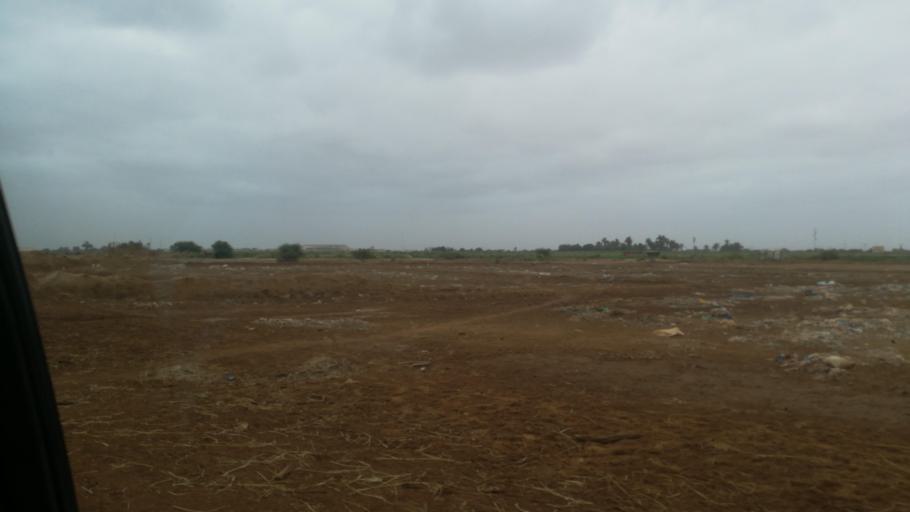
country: SN
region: Saint-Louis
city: Rosso
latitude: 16.2820
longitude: -16.1577
